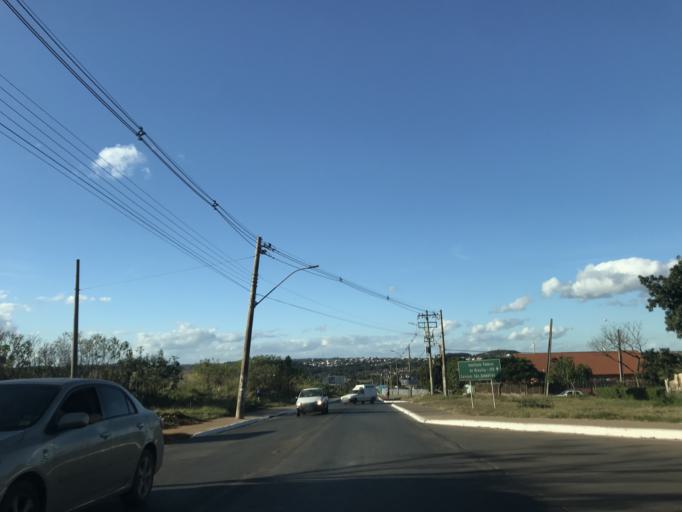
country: BR
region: Federal District
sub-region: Brasilia
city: Brasilia
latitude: -15.8941
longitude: -47.7846
